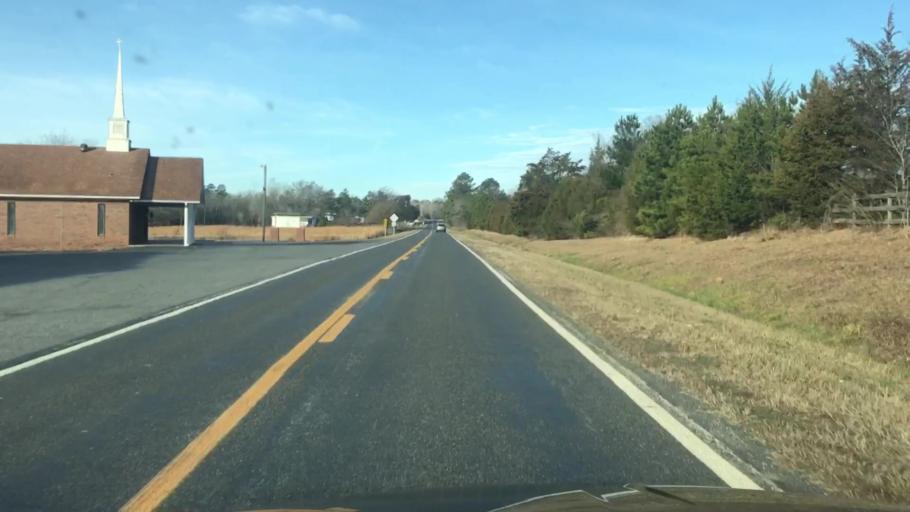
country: US
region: Arkansas
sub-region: Garland County
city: Rockwell
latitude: 34.4711
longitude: -93.2471
